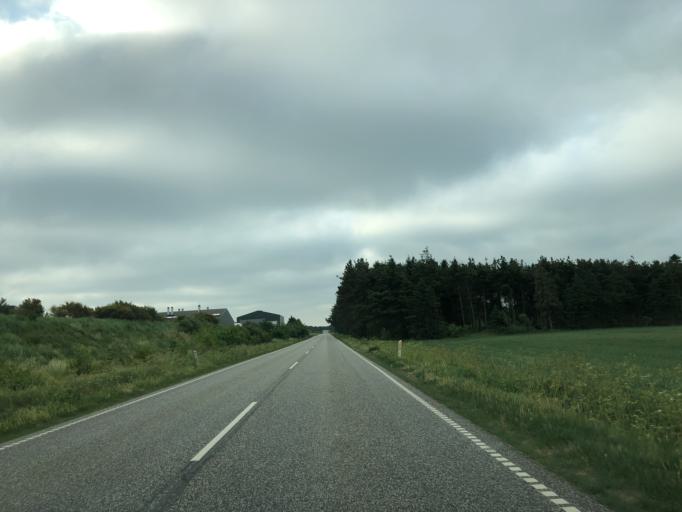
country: DK
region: Central Jutland
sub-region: Ikast-Brande Kommune
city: Brande
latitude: 55.9070
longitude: 9.1911
